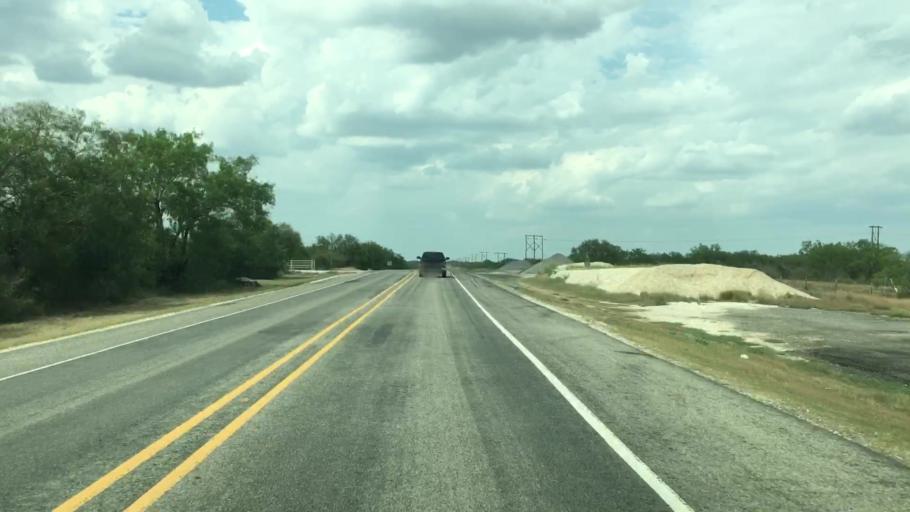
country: US
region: Texas
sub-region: Live Oak County
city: Three Rivers
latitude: 28.6461
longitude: -98.2846
